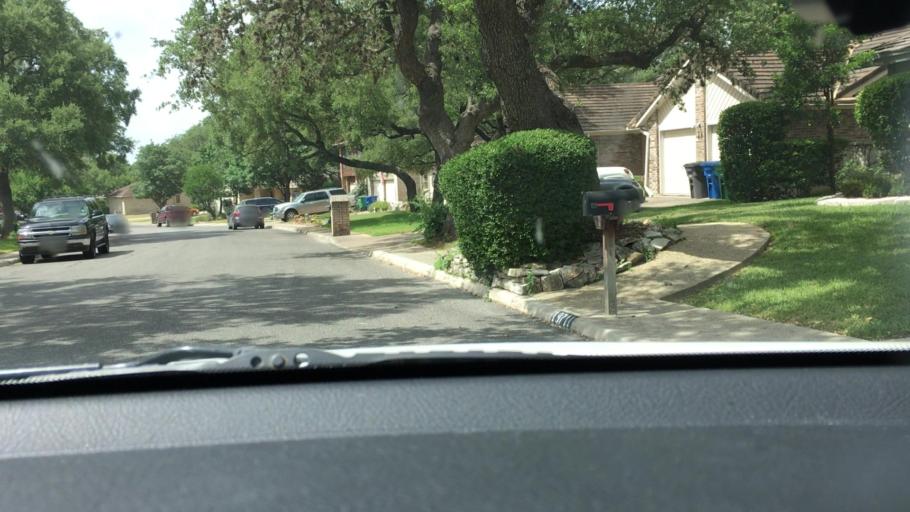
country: US
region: Texas
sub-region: Bexar County
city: Hollywood Park
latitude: 29.6258
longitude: -98.4540
